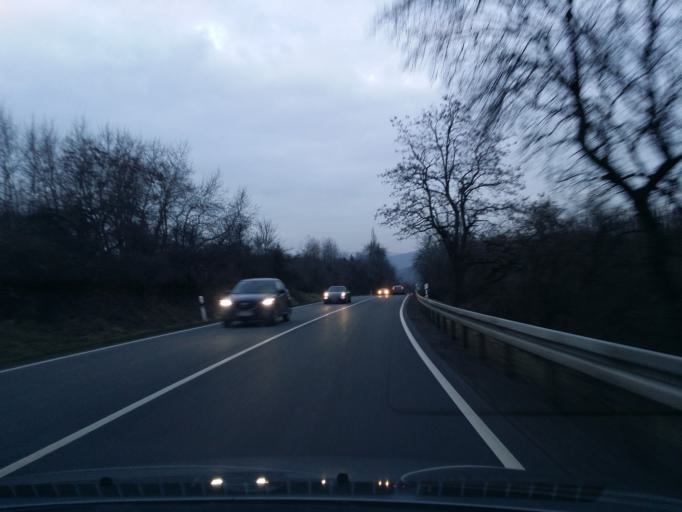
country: DE
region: Hesse
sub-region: Regierungsbezirk Darmstadt
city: Wiesbaden
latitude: 50.1039
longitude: 8.2783
